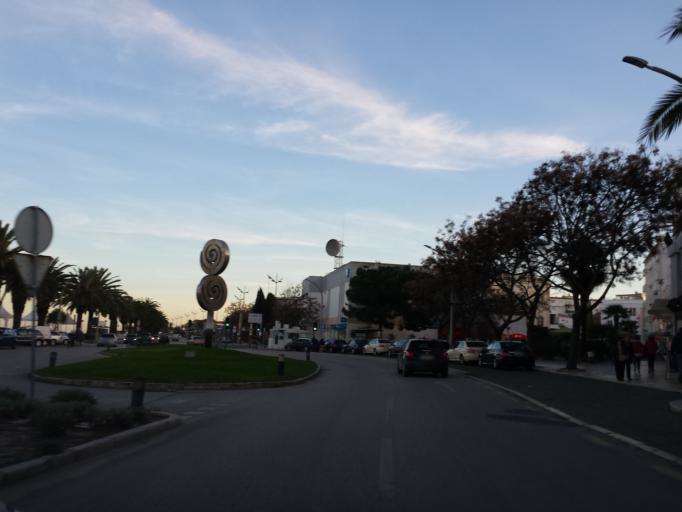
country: PT
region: Faro
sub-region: Lagos
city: Lagos
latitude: 37.1041
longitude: -8.6729
